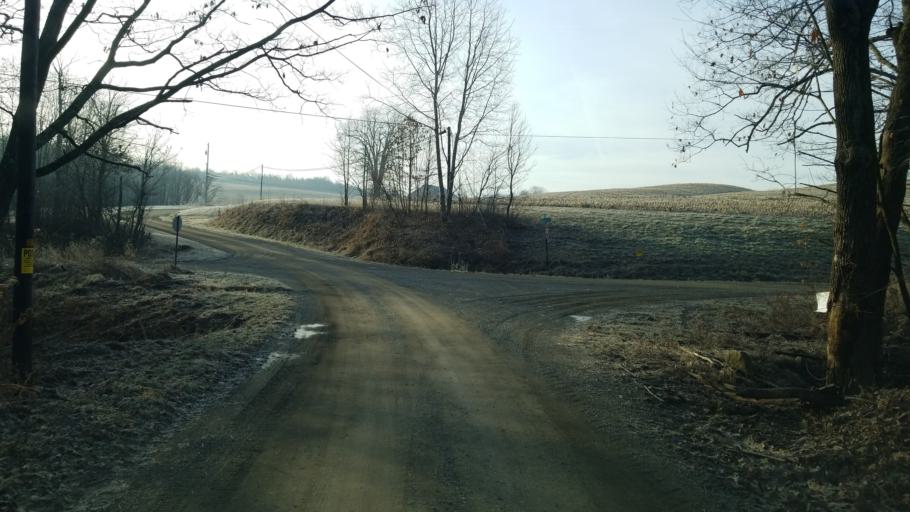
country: US
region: Pennsylvania
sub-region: Indiana County
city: Chevy Chase Heights
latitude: 40.8466
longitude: -79.2484
